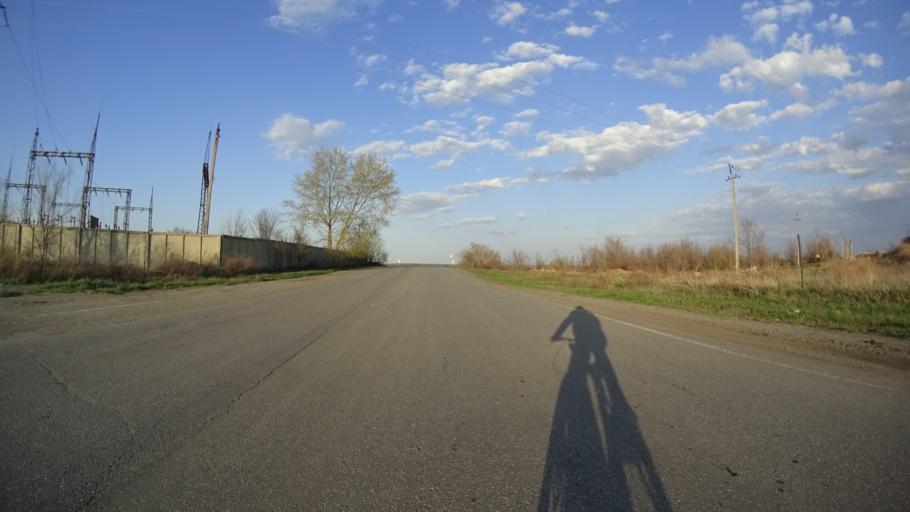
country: RU
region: Chelyabinsk
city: Troitsk
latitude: 54.0623
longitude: 61.5725
